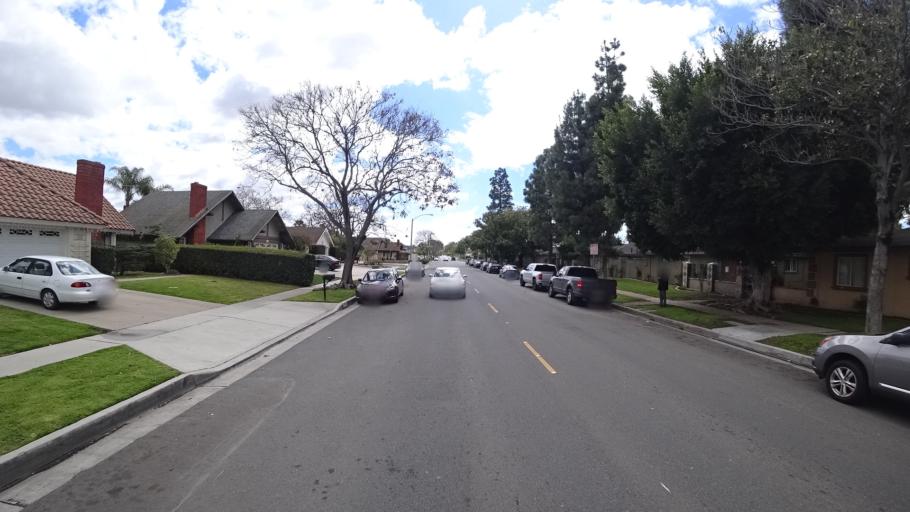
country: US
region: California
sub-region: Orange County
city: Anaheim
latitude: 33.8280
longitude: -117.9371
